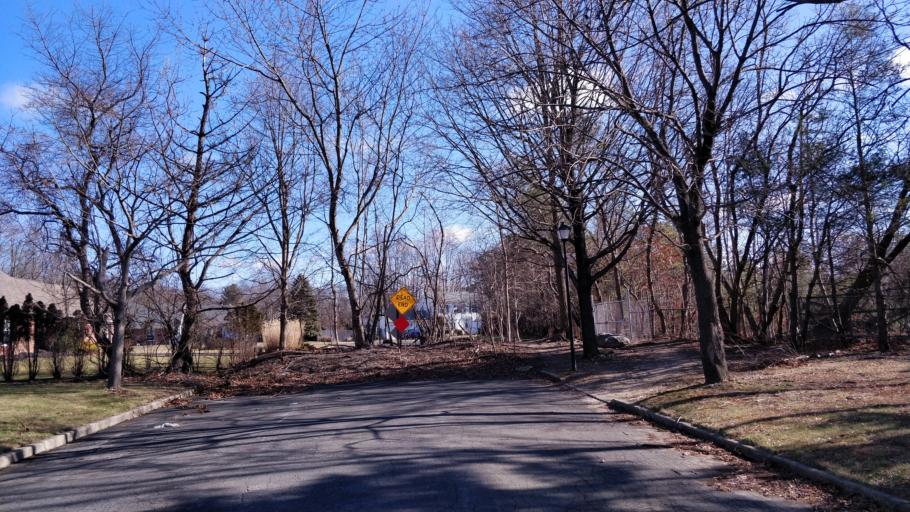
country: US
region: New York
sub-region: Suffolk County
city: Saint James
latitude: 40.8863
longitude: -73.1365
